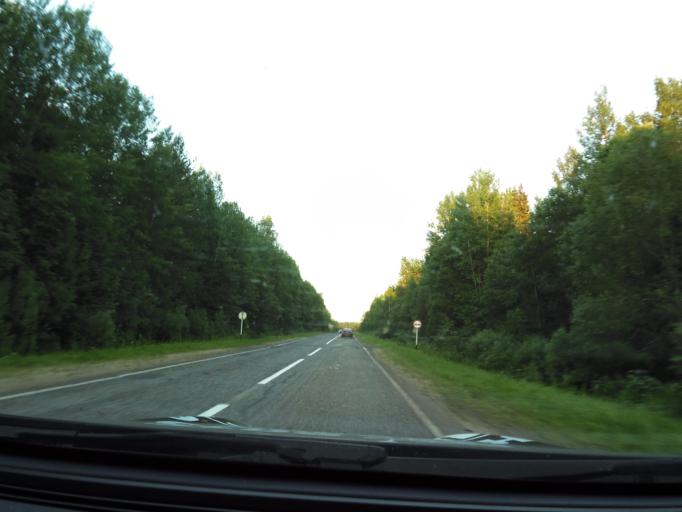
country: RU
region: Jaroslavl
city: Prechistoye
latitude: 58.3836
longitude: 40.4639
